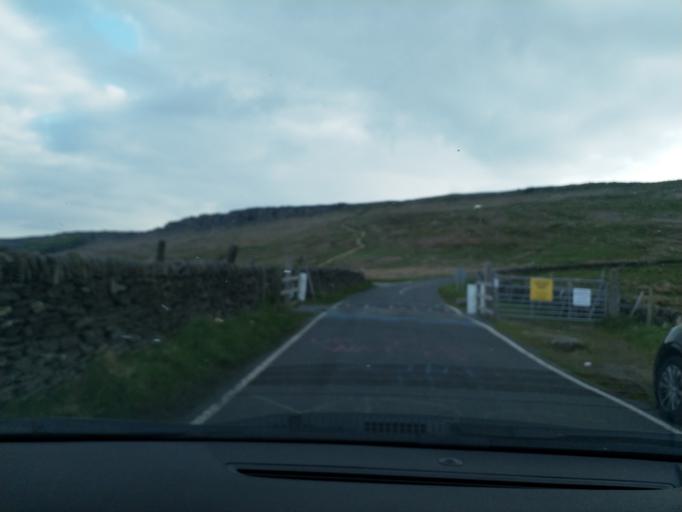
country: GB
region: England
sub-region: Derbyshire
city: Hathersage
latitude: 53.3416
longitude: -1.6337
